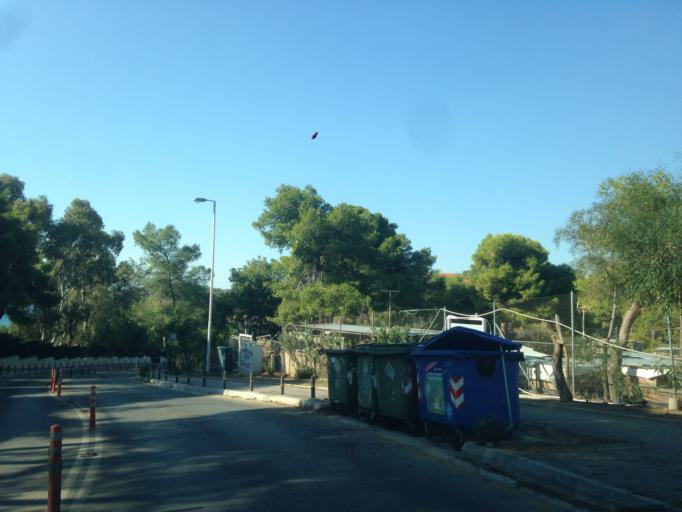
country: GR
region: Attica
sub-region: Nomarchia Anatolikis Attikis
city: Vouliagmeni
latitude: 37.8089
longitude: 23.7752
